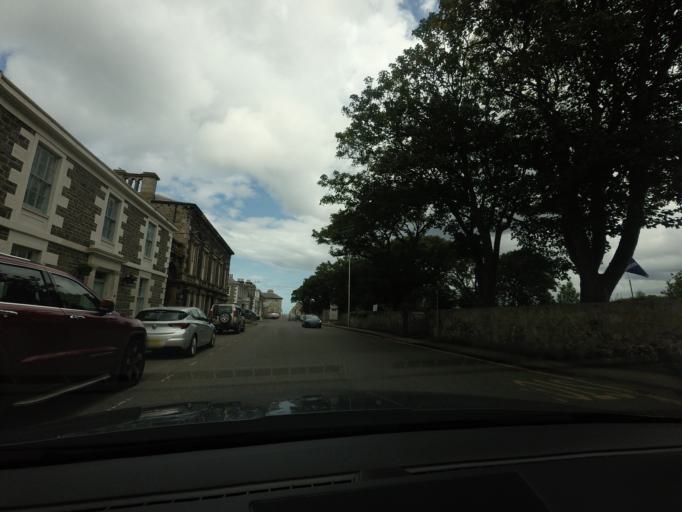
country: GB
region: Scotland
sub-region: Aberdeenshire
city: Banff
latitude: 57.6664
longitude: -2.5237
